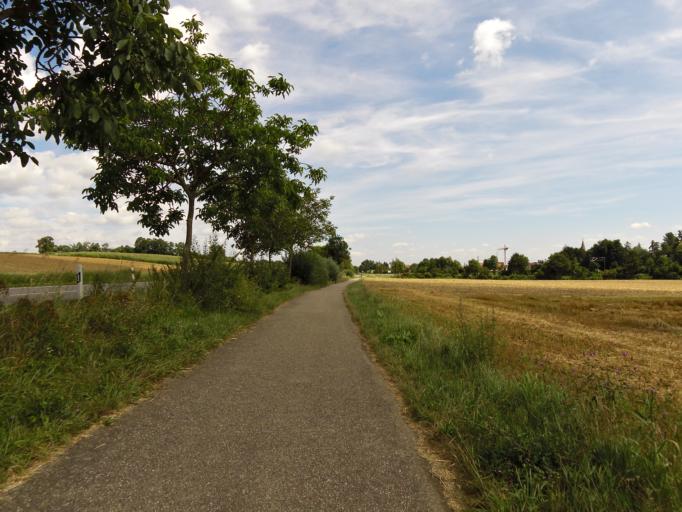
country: DE
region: Rheinland-Pfalz
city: Rulzheim
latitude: 49.1569
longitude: 8.2774
